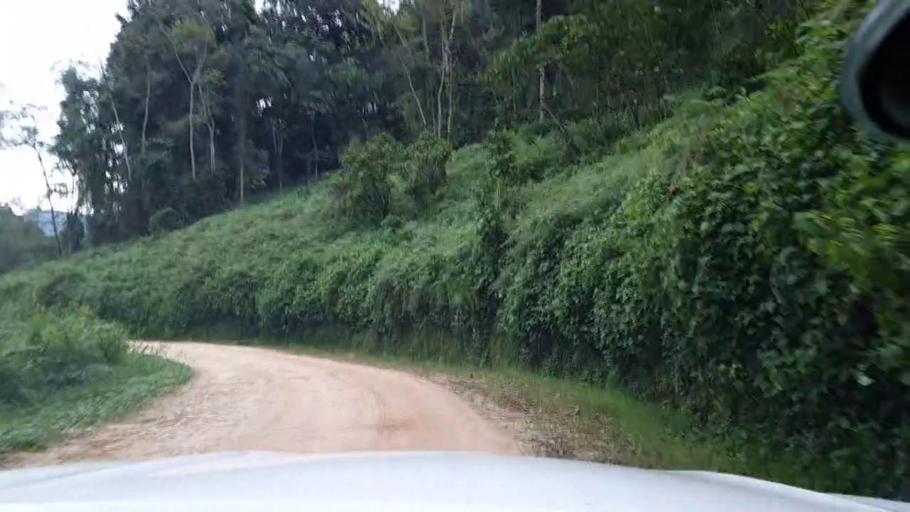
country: RW
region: Western Province
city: Cyangugu
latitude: -2.5584
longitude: 29.2299
